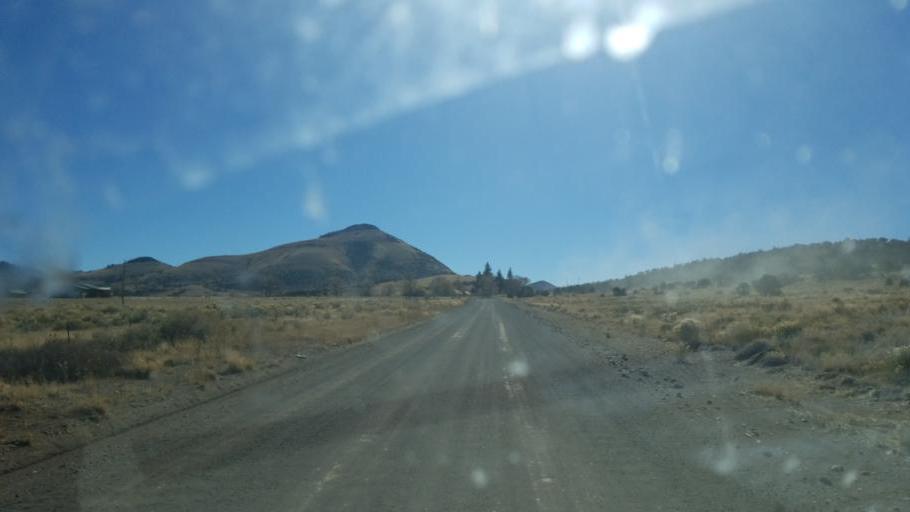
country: US
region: Colorado
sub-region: Rio Grande County
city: Del Norte
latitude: 37.6310
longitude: -106.3638
